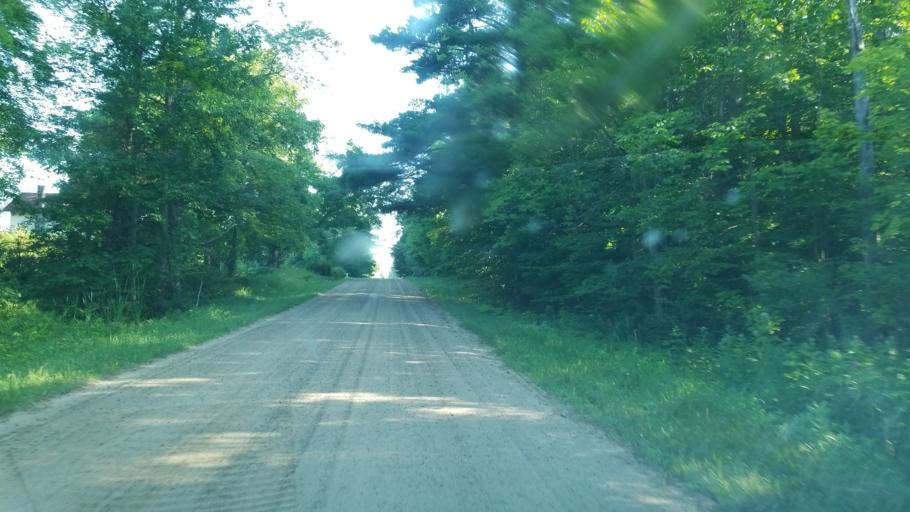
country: US
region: Michigan
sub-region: Mecosta County
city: Canadian Lakes
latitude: 43.5600
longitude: -85.4232
